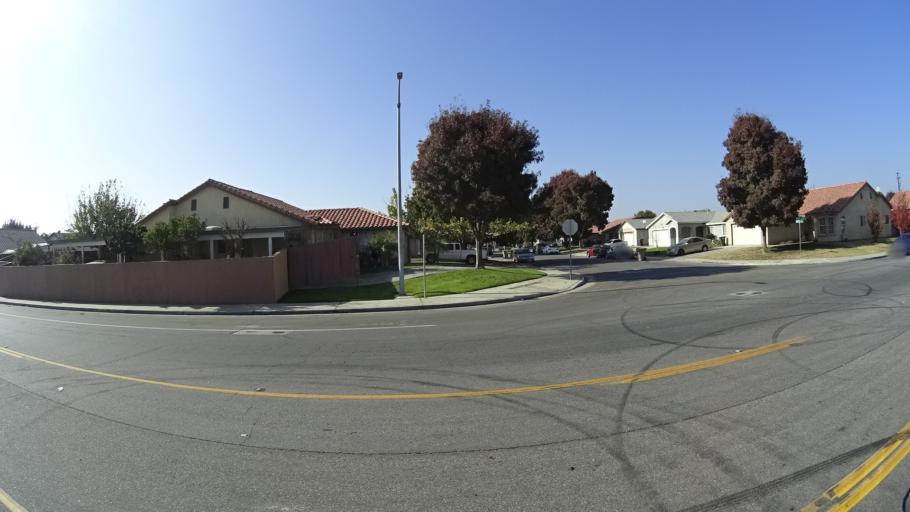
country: US
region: California
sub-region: Kern County
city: Greenfield
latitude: 35.2876
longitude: -119.0119
